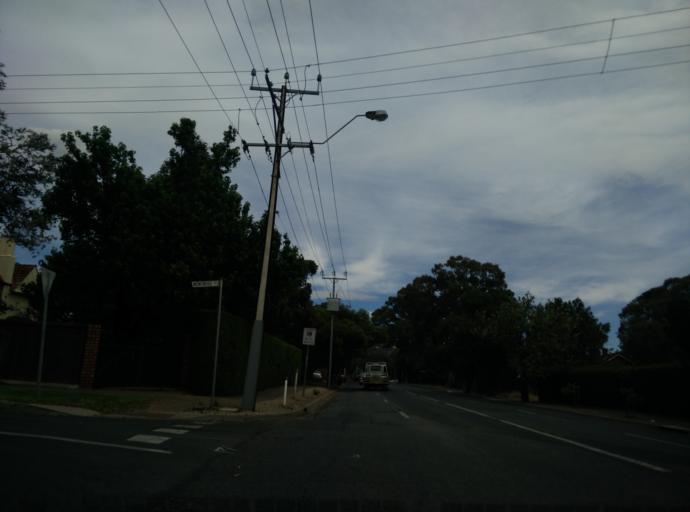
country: AU
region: South Australia
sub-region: Mitcham
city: Mitcham
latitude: -34.9732
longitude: 138.6272
